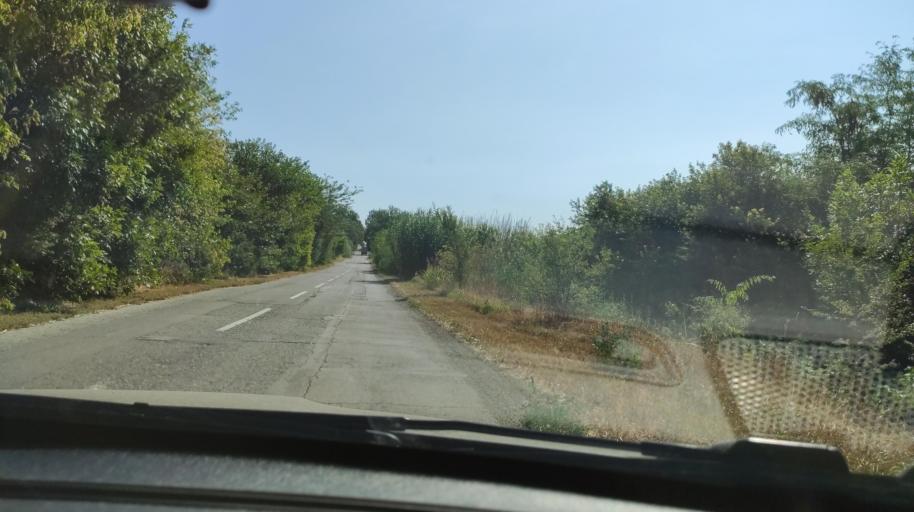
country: RS
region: Autonomna Pokrajina Vojvodina
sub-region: Severnobacki Okrug
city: Backa Topola
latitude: 45.8666
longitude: 19.6109
